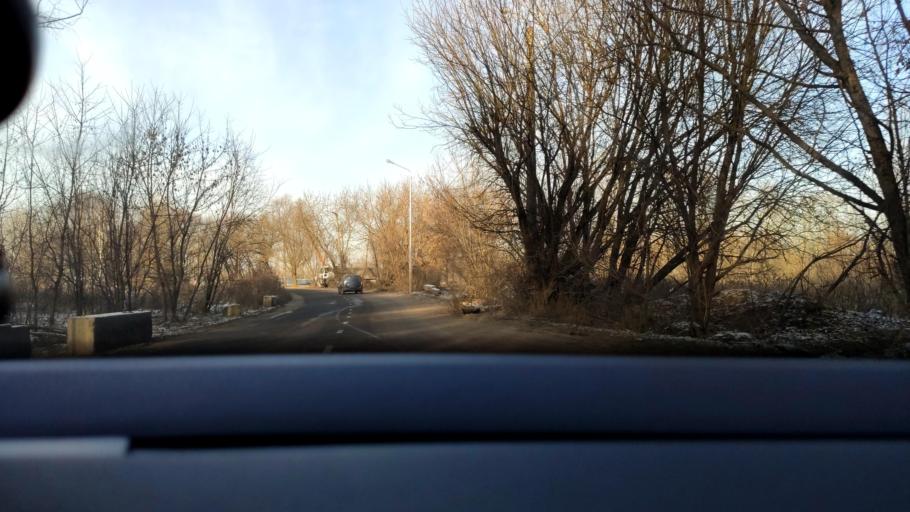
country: RU
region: Moskovskaya
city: Fili
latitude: 55.7511
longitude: 37.4587
